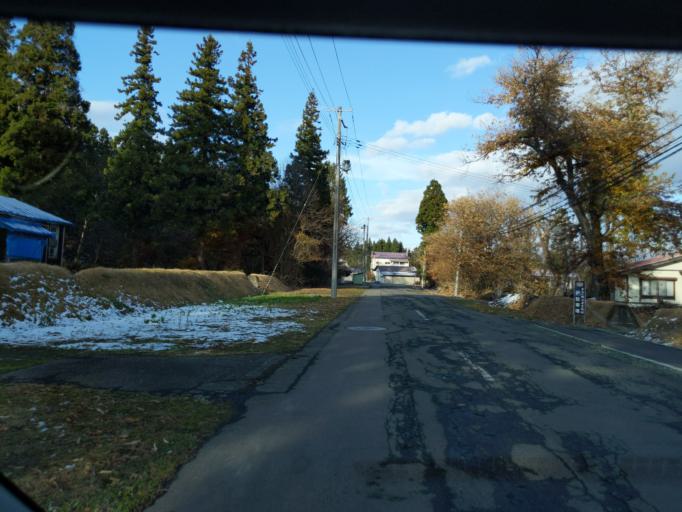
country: JP
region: Iwate
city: Kitakami
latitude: 39.2335
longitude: 141.0506
